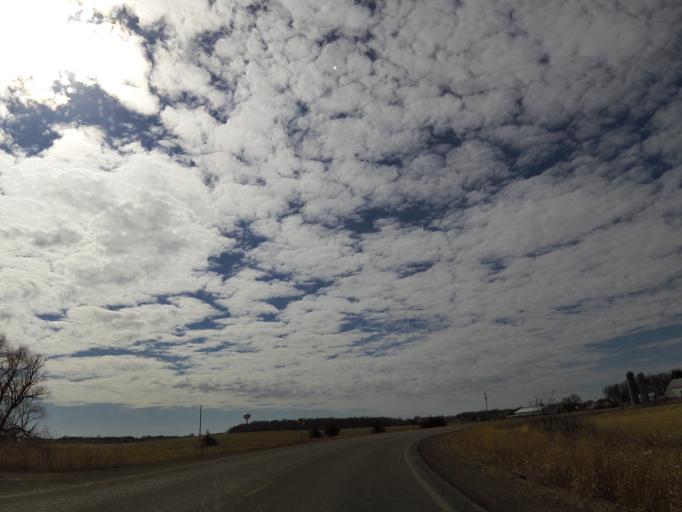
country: US
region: Minnesota
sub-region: Le Sueur County
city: New Prague
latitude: 44.5595
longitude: -93.5567
